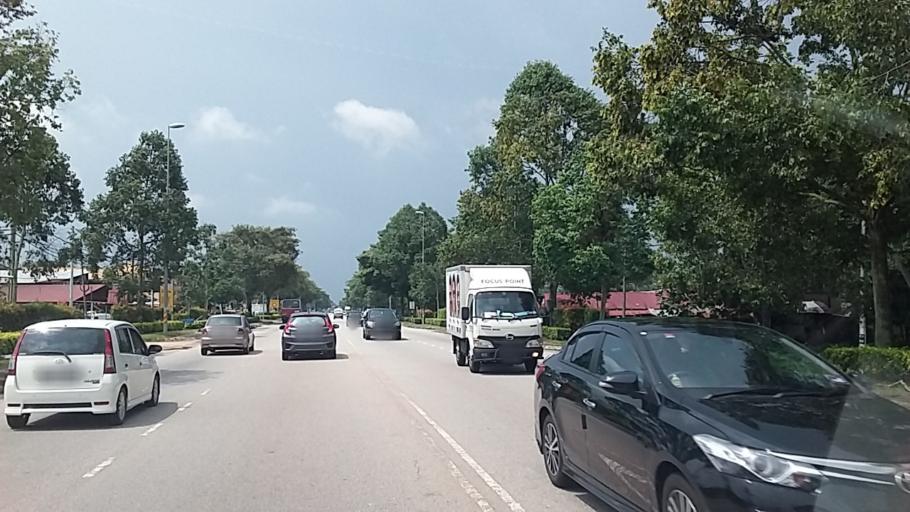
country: MY
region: Johor
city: Parit Raja
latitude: 1.8596
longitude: 103.1027
